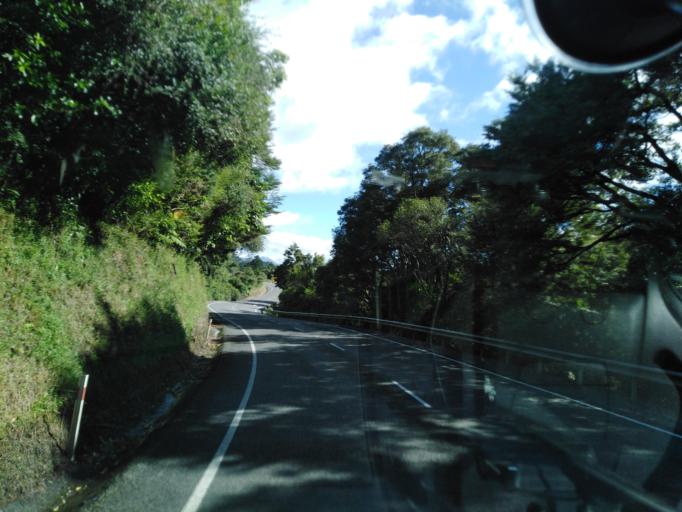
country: NZ
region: Nelson
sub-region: Nelson City
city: Nelson
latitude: -41.2956
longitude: 173.5737
